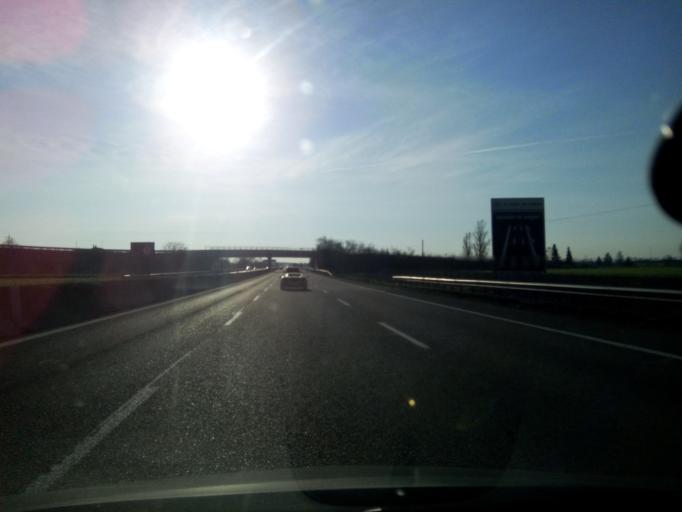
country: IT
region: Emilia-Romagna
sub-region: Provincia di Parma
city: Ponte Taro
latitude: 44.8604
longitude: 10.2532
